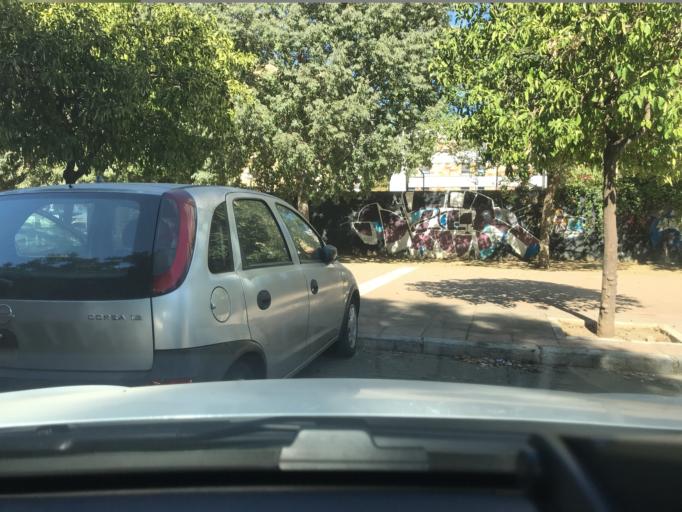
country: ES
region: Andalusia
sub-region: Provincia de Sevilla
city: Sevilla
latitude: 37.3899
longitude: -5.9732
